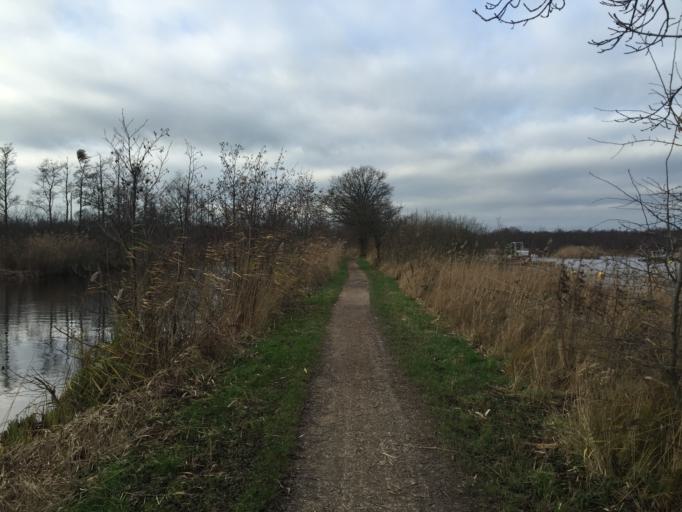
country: NL
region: North Holland
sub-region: Gemeente Wijdemeren
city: Kortenhoef
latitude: 52.2642
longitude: 5.0742
